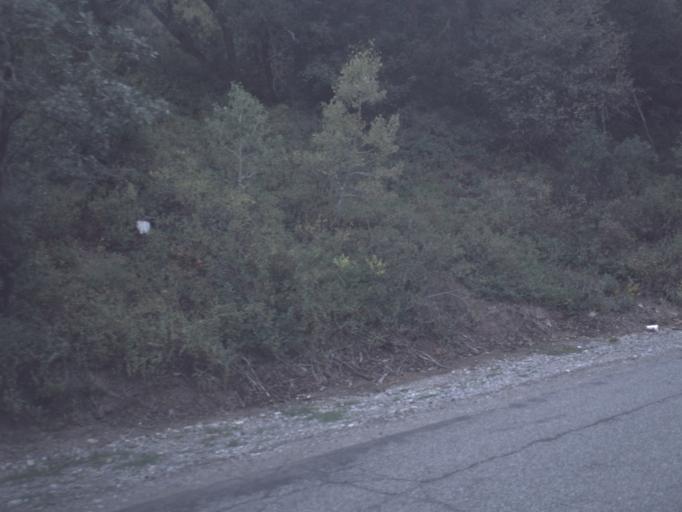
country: US
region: Utah
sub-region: Utah County
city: Lindon
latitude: 40.3937
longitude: -111.5819
